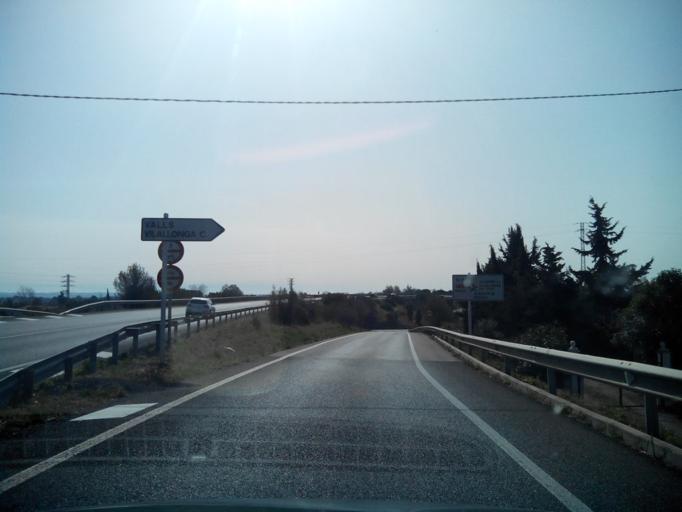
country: ES
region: Catalonia
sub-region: Provincia de Tarragona
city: Alcover
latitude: 41.2649
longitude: 1.1761
